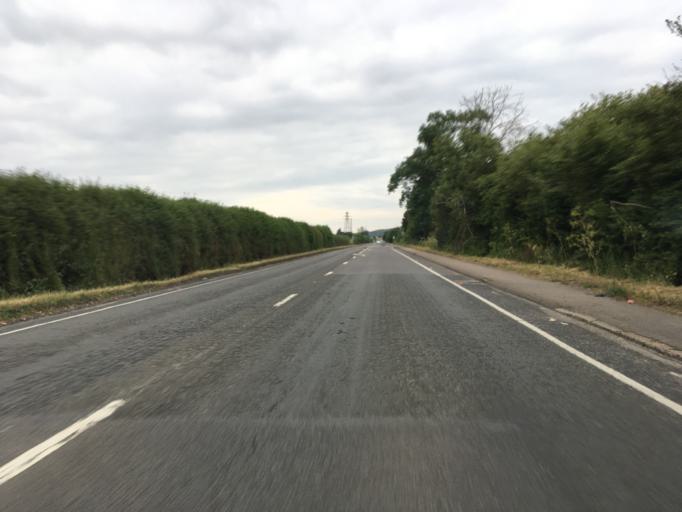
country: GB
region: England
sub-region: Hertfordshire
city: Markyate
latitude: 51.8557
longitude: -0.4795
